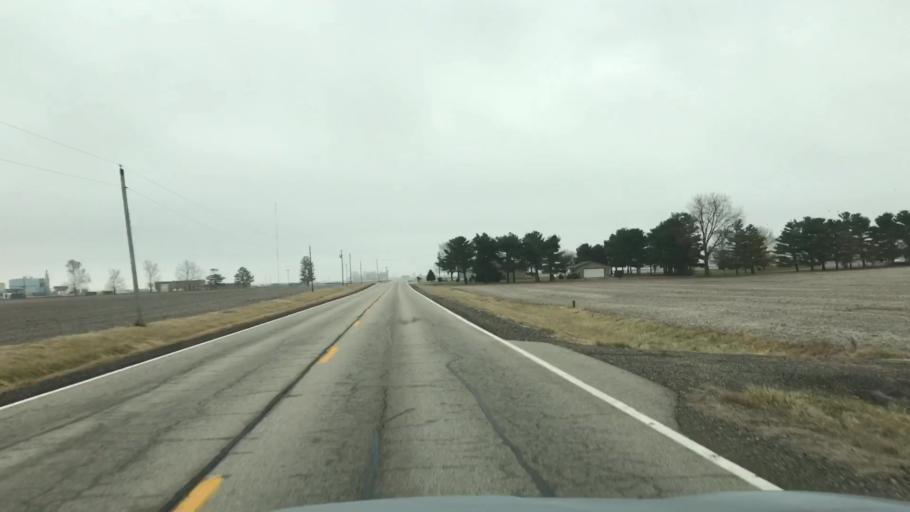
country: US
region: Illinois
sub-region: McLean County
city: Hudson
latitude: 40.5876
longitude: -88.9448
